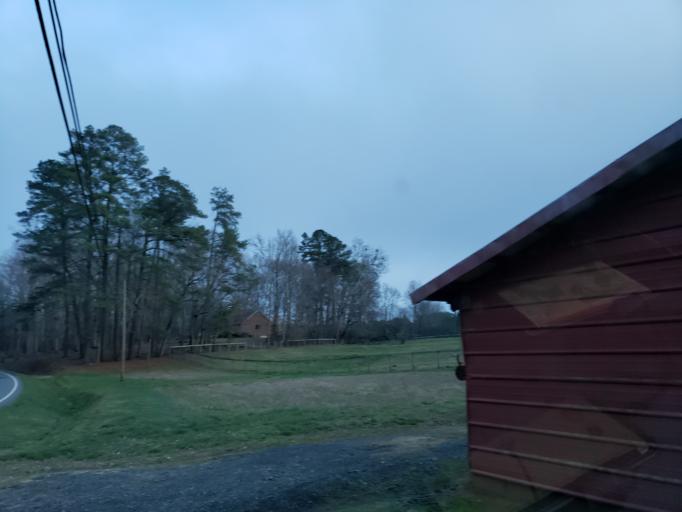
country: US
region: Georgia
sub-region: Fulton County
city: Milton
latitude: 34.2293
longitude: -84.3302
